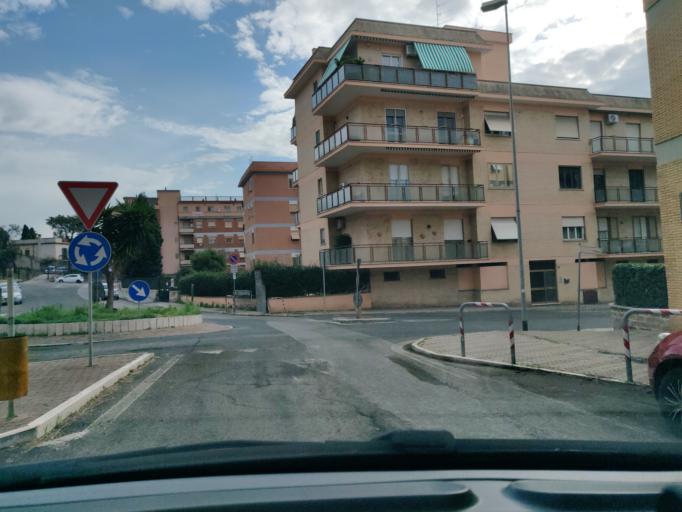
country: IT
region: Latium
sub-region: Citta metropolitana di Roma Capitale
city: Civitavecchia
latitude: 42.0941
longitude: 11.8085
